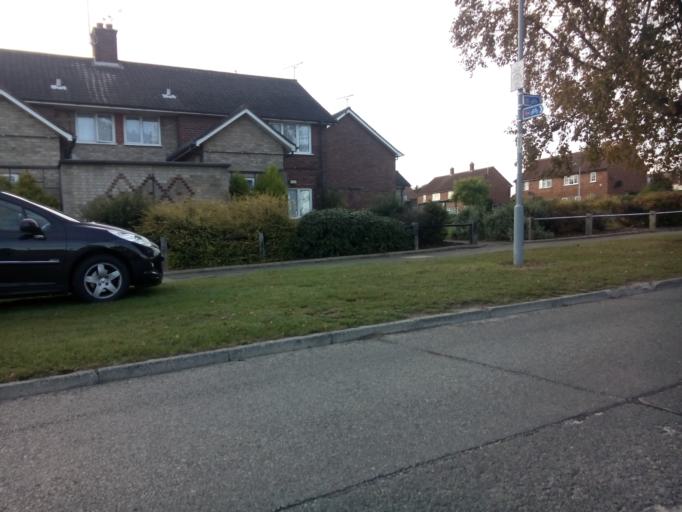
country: GB
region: England
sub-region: Suffolk
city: Ipswich
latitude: 52.0801
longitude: 1.1360
